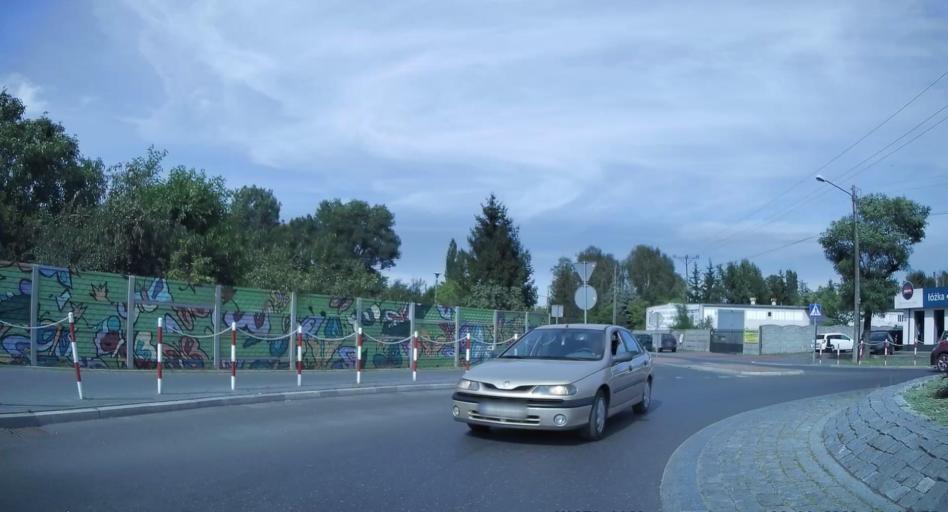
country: PL
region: Lodz Voivodeship
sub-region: Powiat tomaszowski
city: Tomaszow Mazowiecki
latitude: 51.5357
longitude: 19.9967
